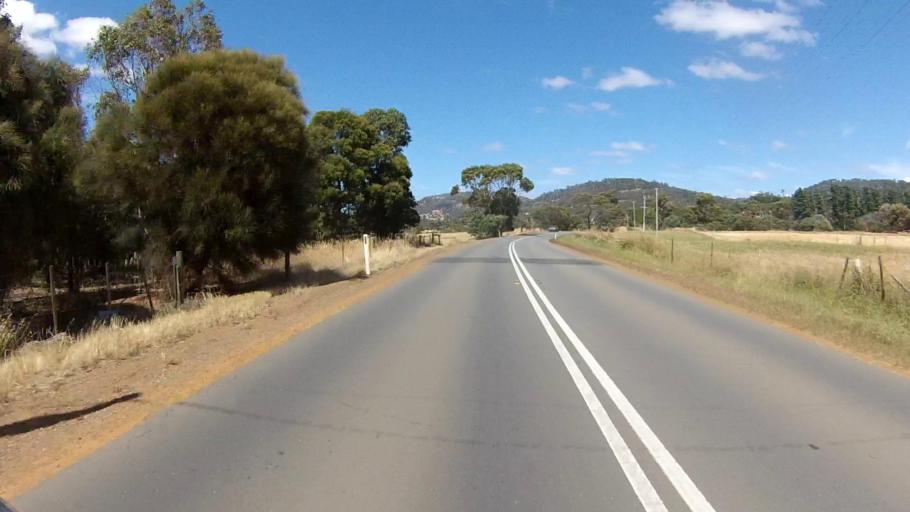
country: AU
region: Tasmania
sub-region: Clarence
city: Cambridge
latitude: -42.7699
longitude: 147.4162
